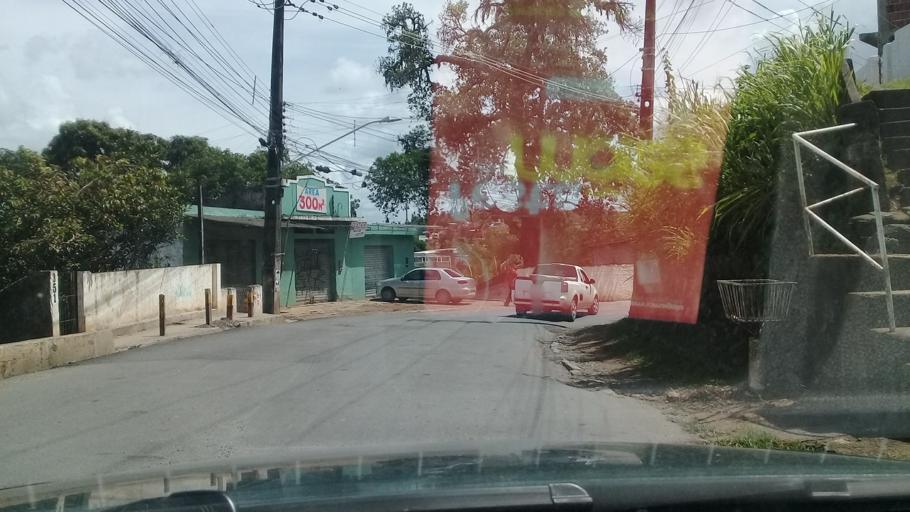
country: BR
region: Pernambuco
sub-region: Jaboatao Dos Guararapes
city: Jaboatao dos Guararapes
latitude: -8.1071
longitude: -35.0176
